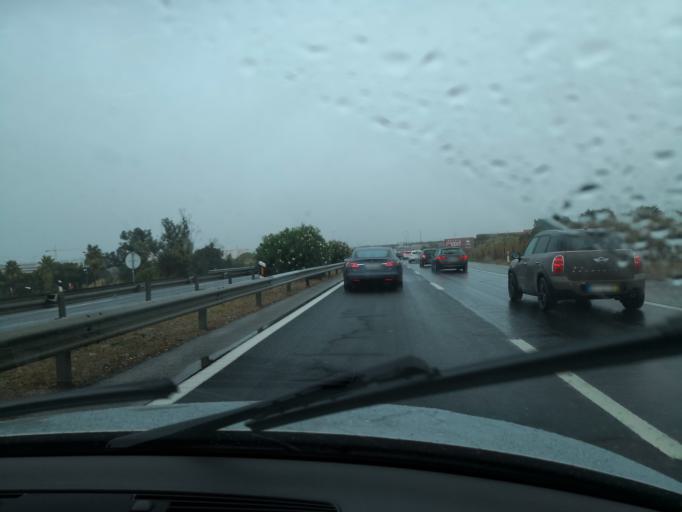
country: PT
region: Setubal
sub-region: Montijo
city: Montijo
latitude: 38.6960
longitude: -8.9395
